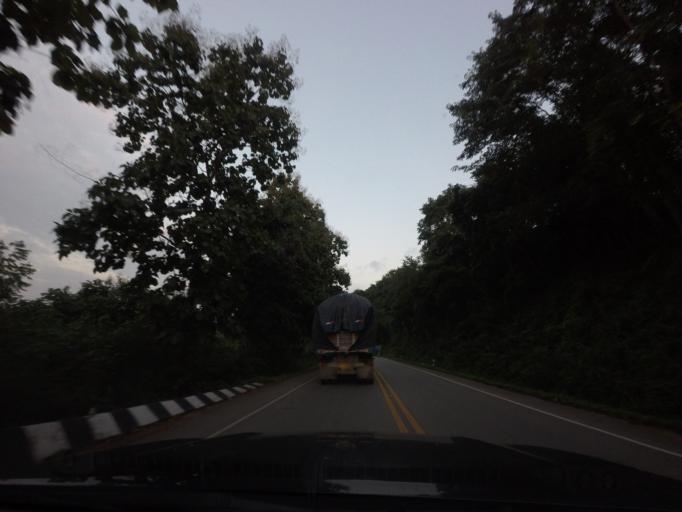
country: TH
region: Nan
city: Wiang Sa
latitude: 18.4774
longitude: 100.7238
